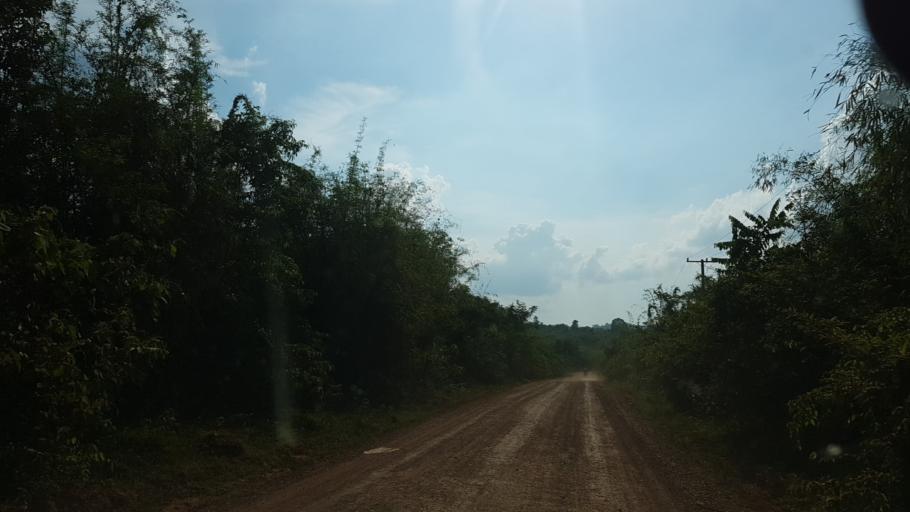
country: LA
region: Vientiane
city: Muang Phon-Hong
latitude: 18.3471
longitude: 102.2867
